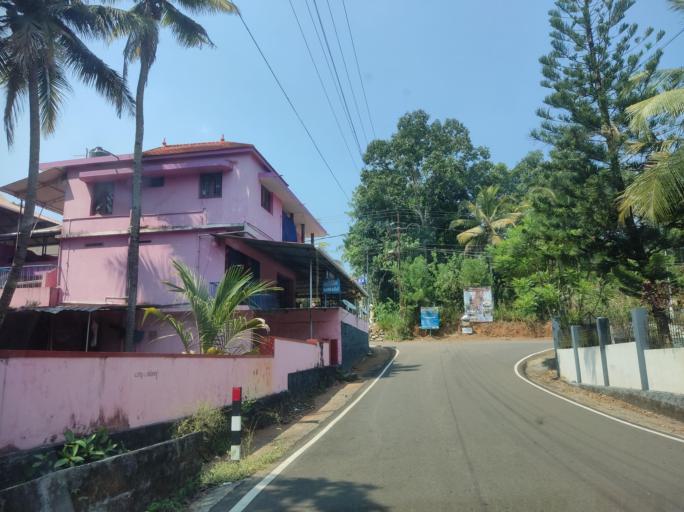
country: IN
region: Kerala
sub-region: Pattanamtitta
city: Adur
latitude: 9.1527
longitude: 76.7249
